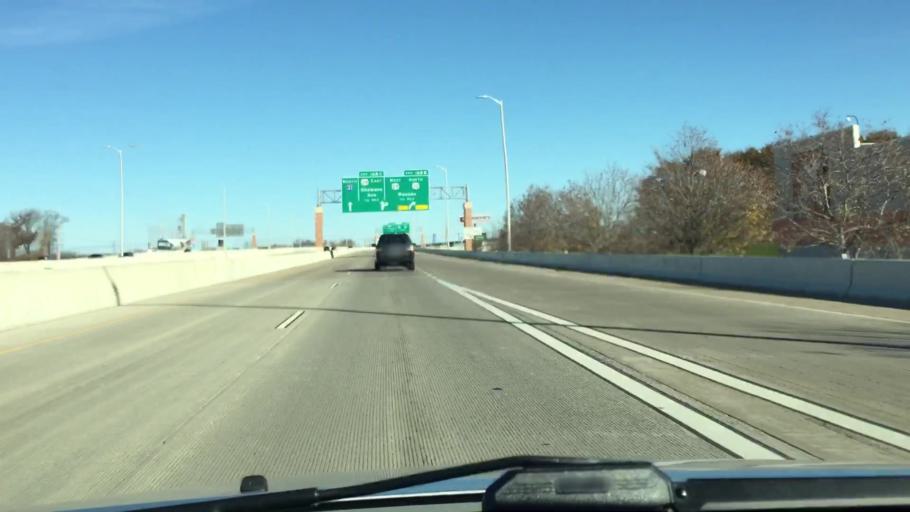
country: US
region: Wisconsin
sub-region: Brown County
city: Howard
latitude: 44.5286
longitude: -88.0814
